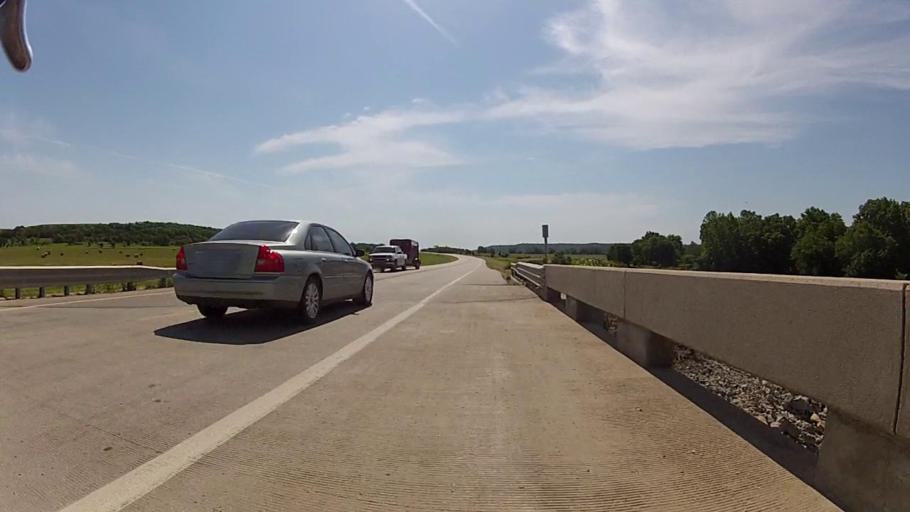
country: US
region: Kansas
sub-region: Chautauqua County
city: Sedan
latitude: 37.1083
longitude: -96.5863
